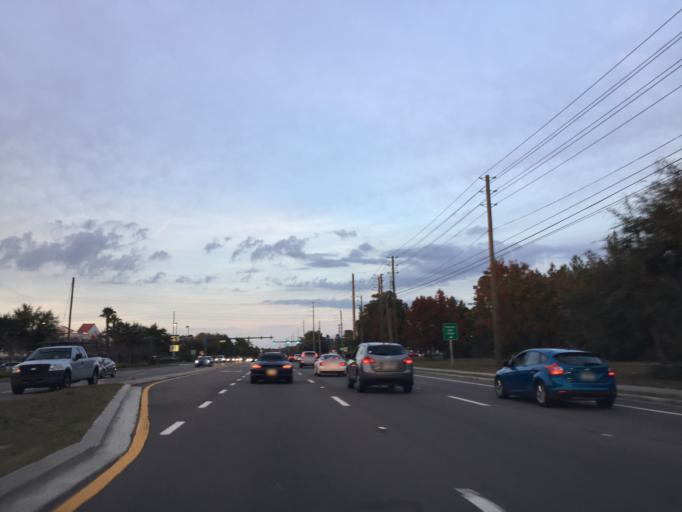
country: US
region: Florida
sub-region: Orange County
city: Alafaya
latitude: 28.6096
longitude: -81.2076
